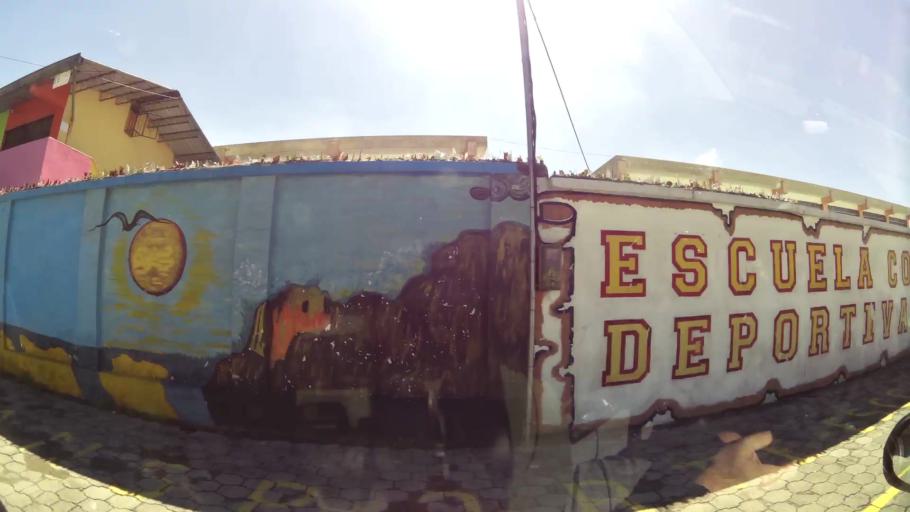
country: EC
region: Pichincha
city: Quito
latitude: -0.2546
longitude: -78.5355
